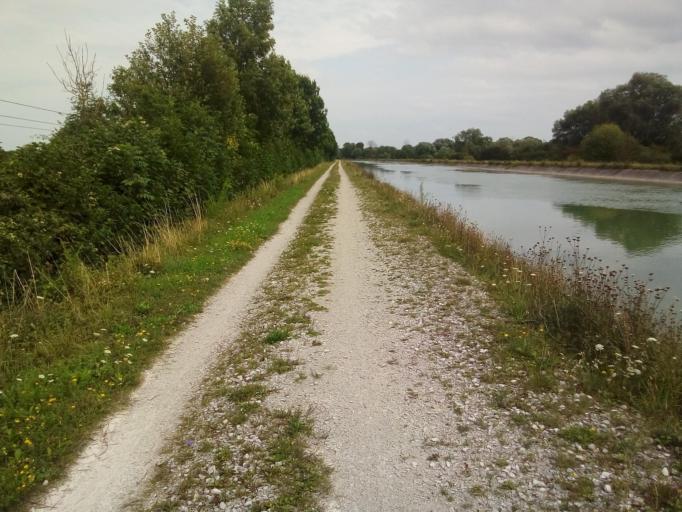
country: DE
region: Bavaria
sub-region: Upper Bavaria
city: Ismaning
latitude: 48.2059
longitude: 11.6784
